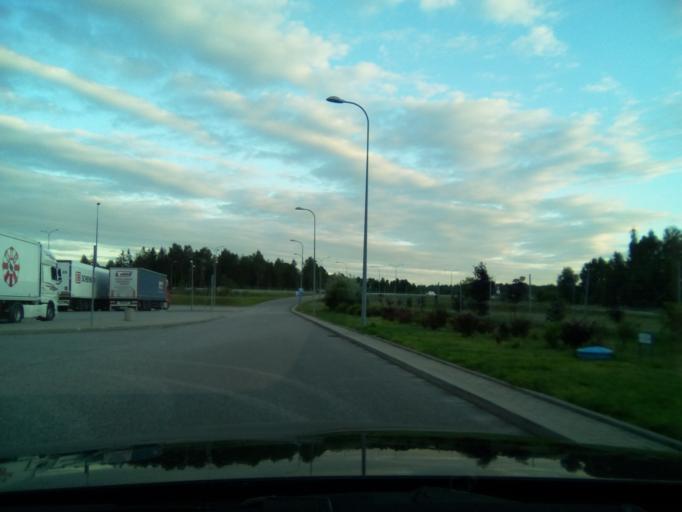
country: PL
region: Lodz Voivodeship
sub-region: powiat Lowicki
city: Bobrowniki
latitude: 52.0283
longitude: 20.0010
